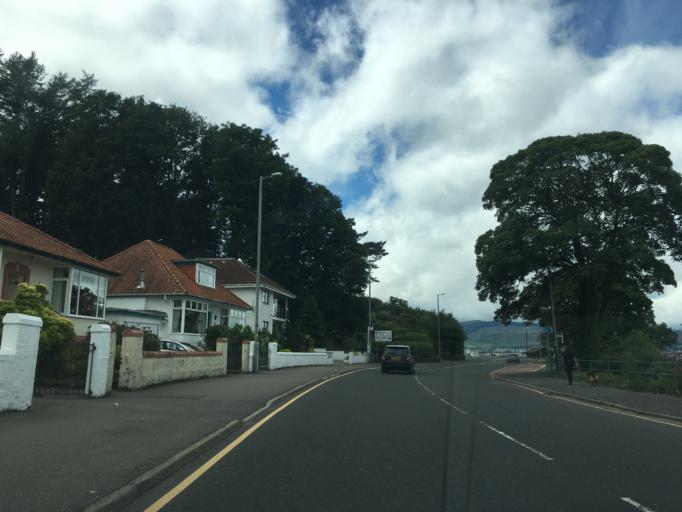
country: GB
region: Scotland
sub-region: Inverclyde
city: Gourock
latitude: 55.9509
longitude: -4.8506
